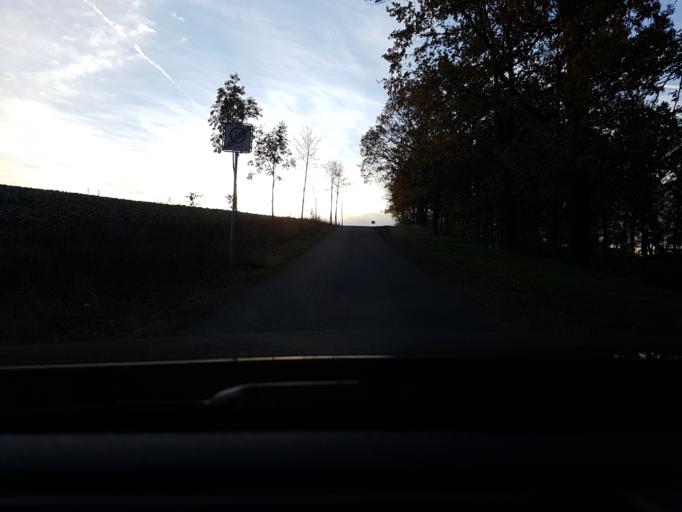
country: DE
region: Saxony
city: Altmittweida
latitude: 50.9651
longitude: 12.9645
